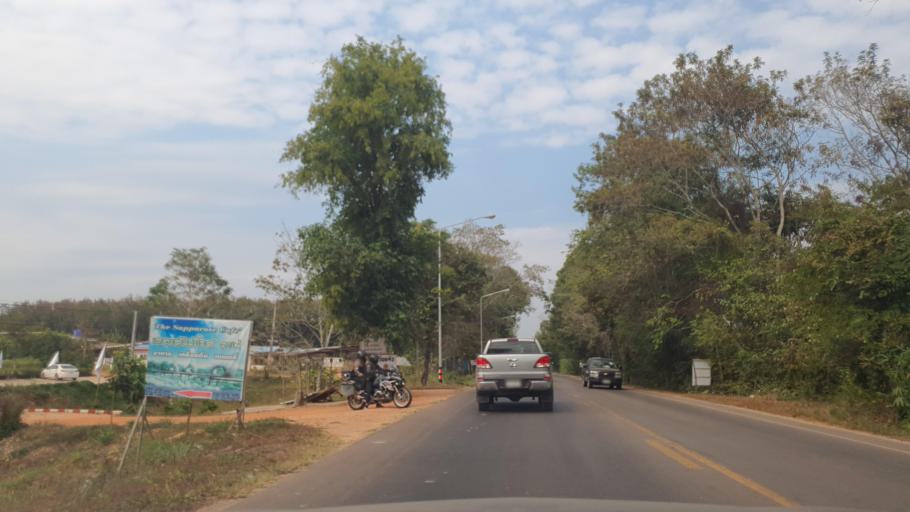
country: TH
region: Changwat Bueng Kan
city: Si Wilai
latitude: 18.2763
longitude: 103.8317
